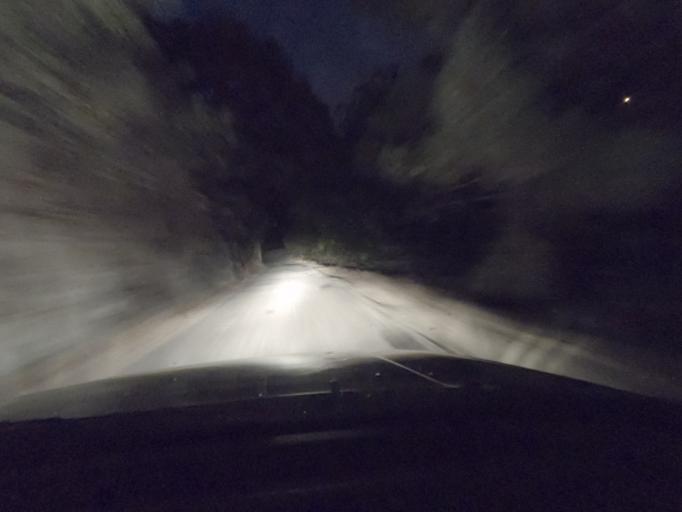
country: PT
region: Vila Real
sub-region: Santa Marta de Penaguiao
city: Santa Marta de Penaguiao
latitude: 41.2051
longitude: -7.8455
